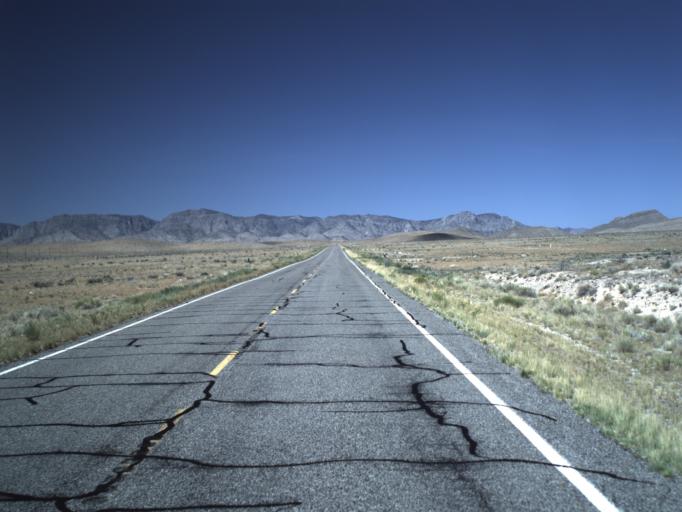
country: US
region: Utah
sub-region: Beaver County
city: Milford
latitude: 39.0384
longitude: -113.3125
